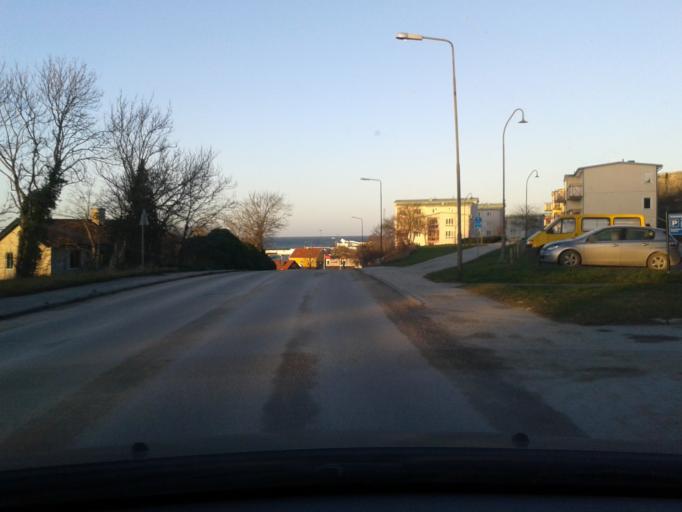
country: SE
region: Gotland
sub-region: Gotland
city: Visby
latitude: 57.6295
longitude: 18.2802
